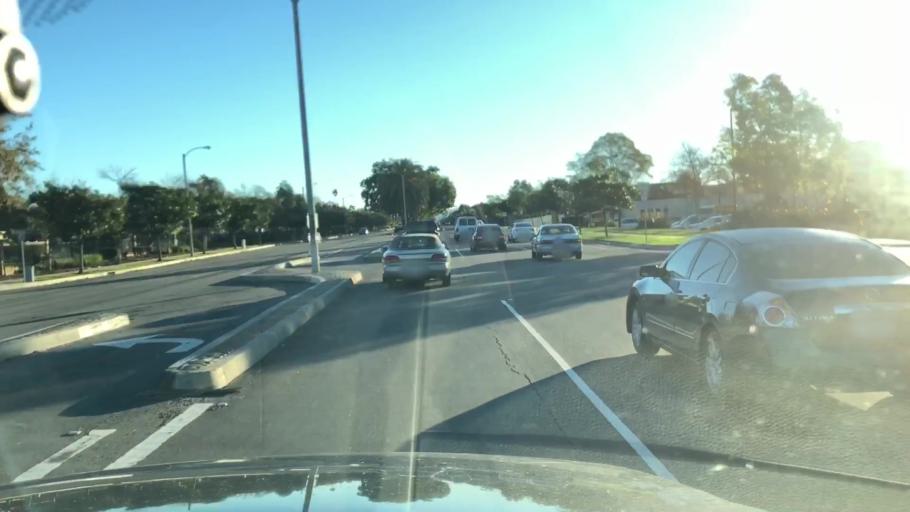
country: US
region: California
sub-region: Ventura County
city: El Rio
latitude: 34.2190
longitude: -119.1705
